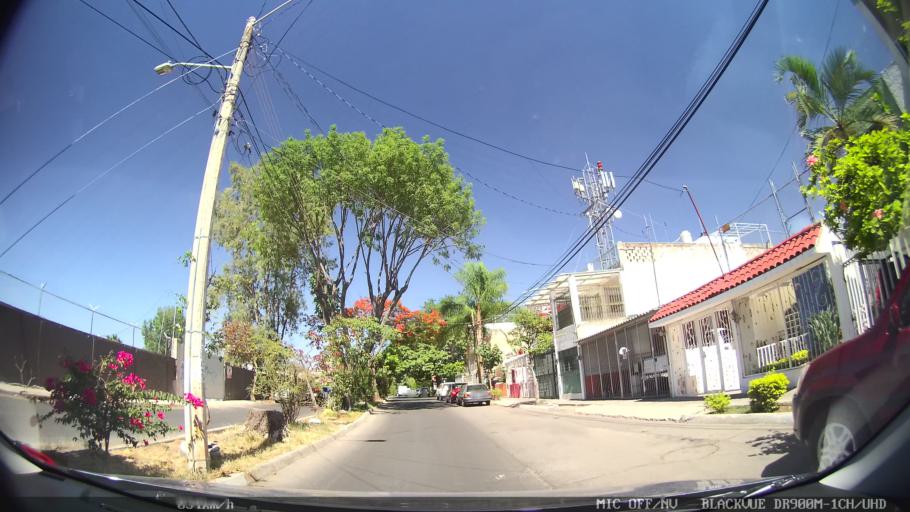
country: MX
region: Jalisco
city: Tlaquepaque
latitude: 20.6483
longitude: -103.2953
